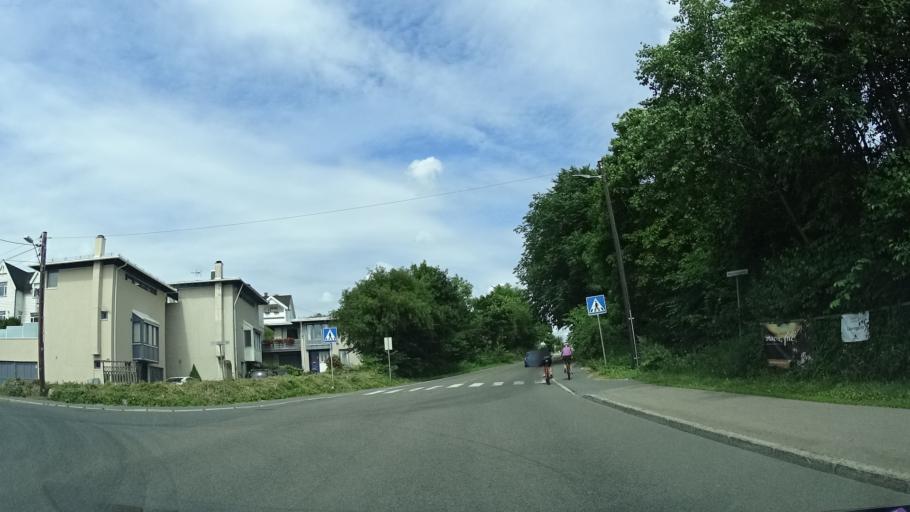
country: NO
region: Oslo
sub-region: Oslo
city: Oslo
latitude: 59.9579
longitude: 10.7638
